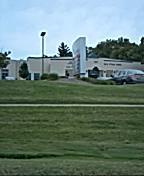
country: US
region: Kentucky
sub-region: Jefferson County
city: Middletown
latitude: 38.2487
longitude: -85.5332
